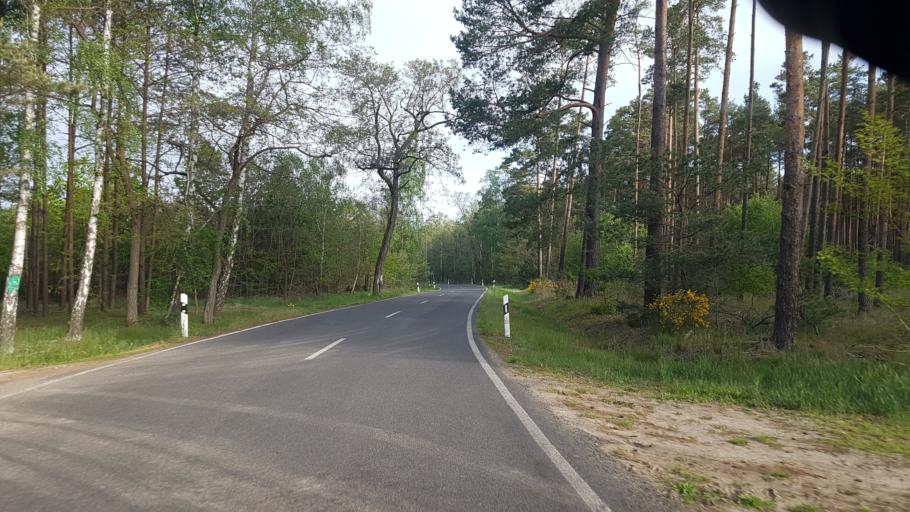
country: DE
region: Brandenburg
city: Dahme
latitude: 51.9249
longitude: 13.4675
